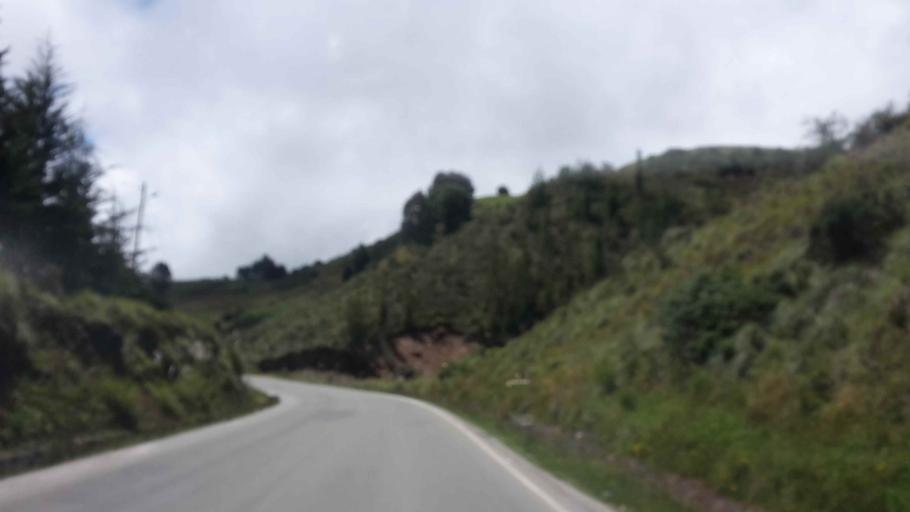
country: BO
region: Cochabamba
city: Colomi
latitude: -17.2567
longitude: -65.8918
